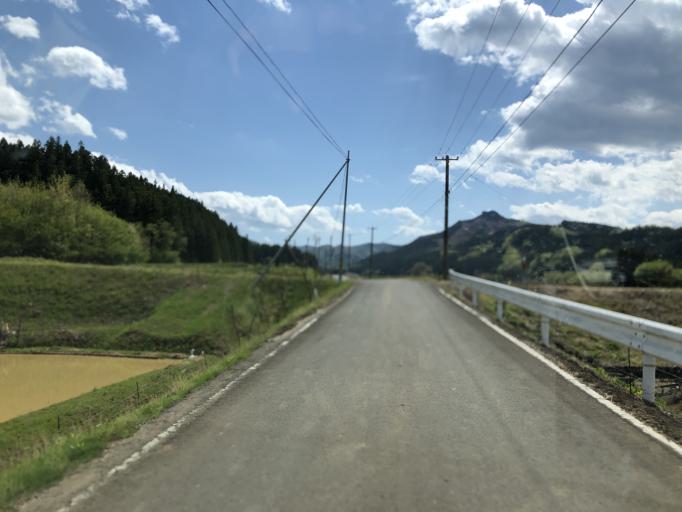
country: JP
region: Fukushima
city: Ishikawa
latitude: 37.0060
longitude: 140.3324
